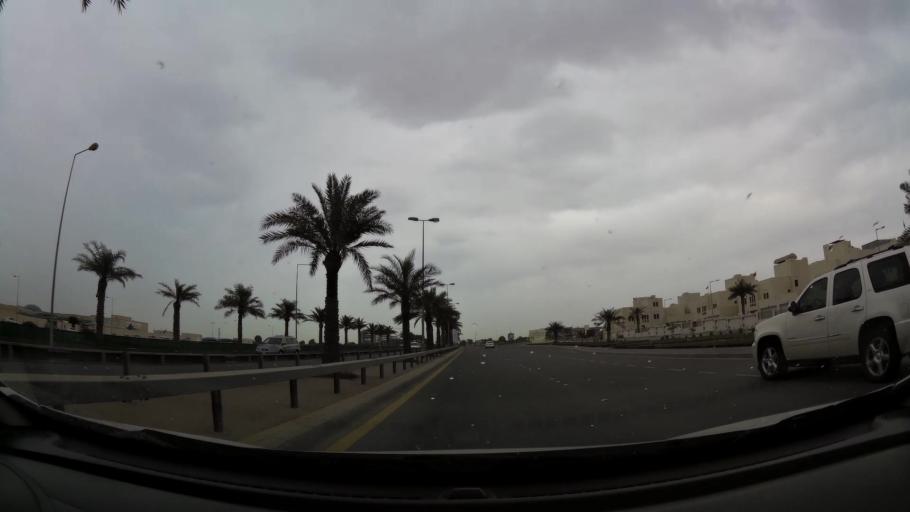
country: BH
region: Northern
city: Ar Rifa'
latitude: 26.1008
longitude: 50.5434
